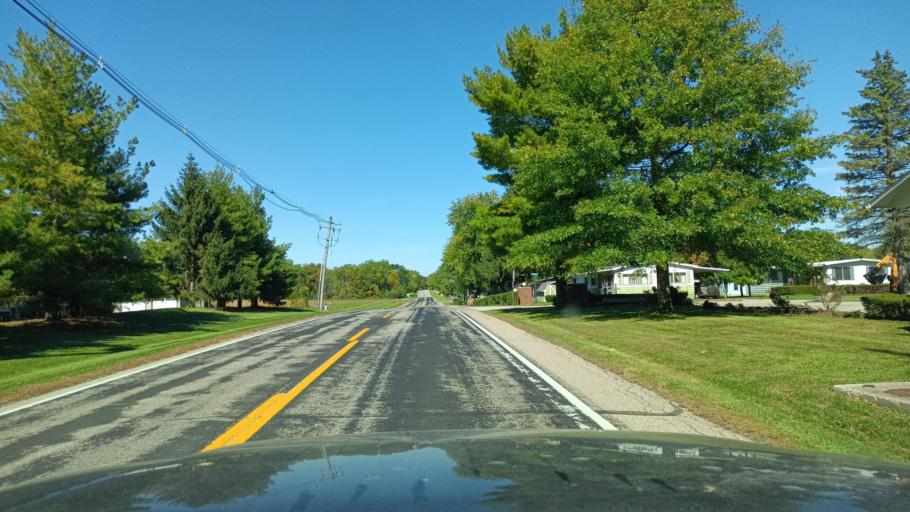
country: US
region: Illinois
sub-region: Champaign County
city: Lake of the Woods
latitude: 40.2050
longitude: -88.3653
